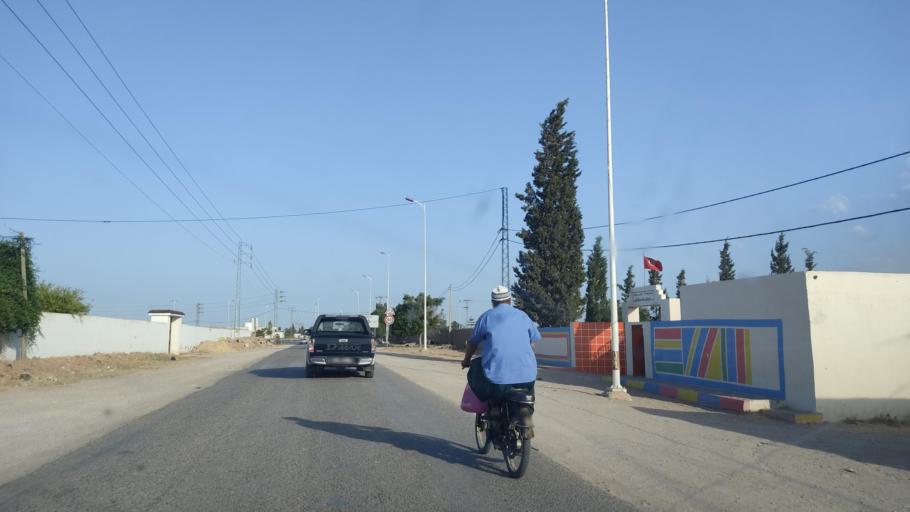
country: TN
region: Safaqis
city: Sfax
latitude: 34.7982
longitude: 10.6773
